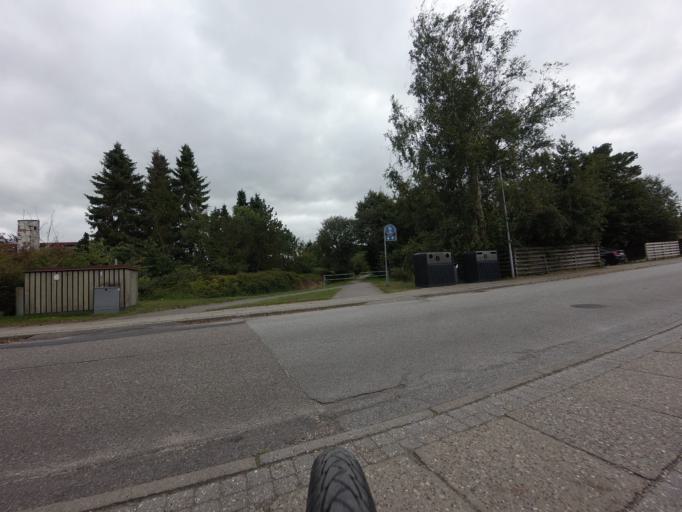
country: DK
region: Central Jutland
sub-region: Ikast-Brande Kommune
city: Brande
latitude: 55.9371
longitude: 9.1422
